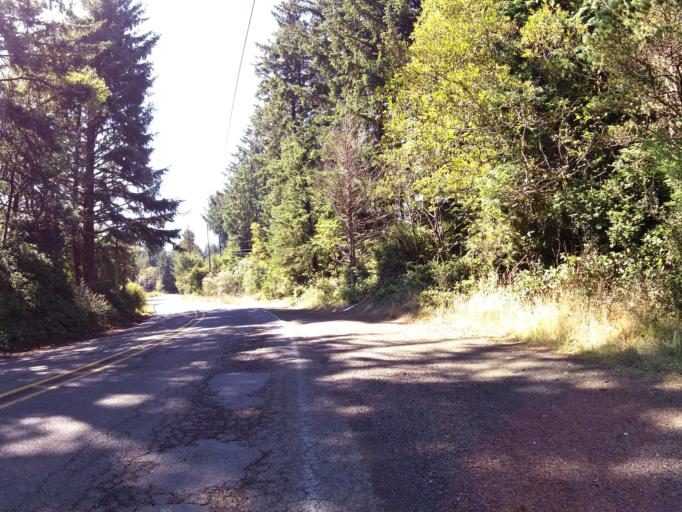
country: US
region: Oregon
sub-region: Coos County
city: Barview
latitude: 43.3314
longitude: -124.3369
